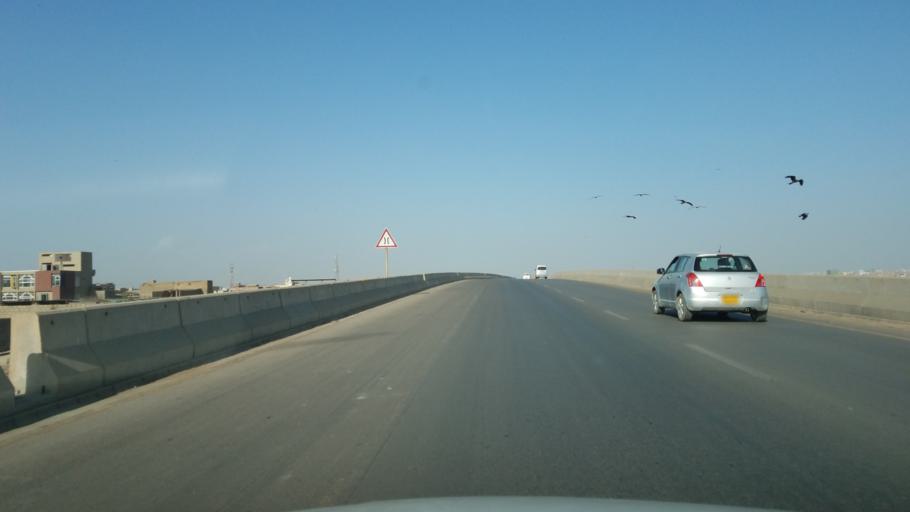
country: PK
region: Sindh
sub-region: Karachi District
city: Karachi
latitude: 24.8811
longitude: 66.9927
